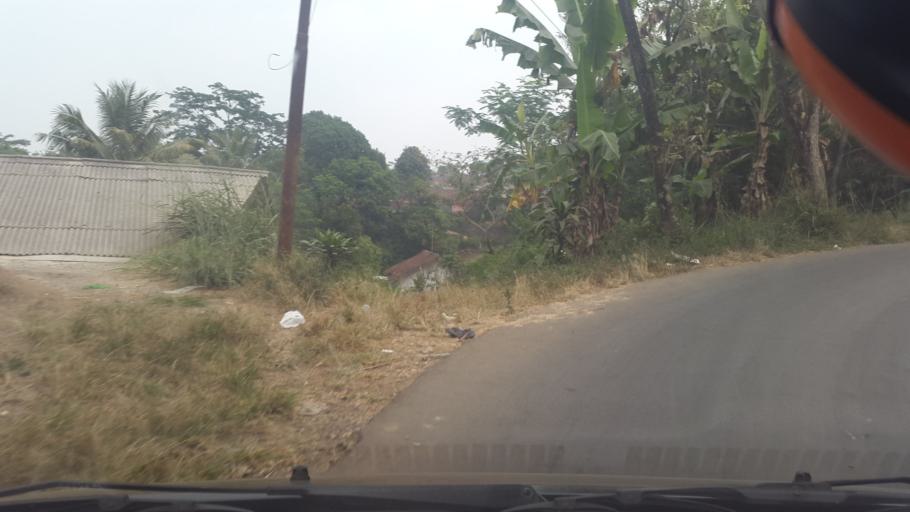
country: ID
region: West Java
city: Sukabumi
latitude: -6.8640
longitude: 106.8908
